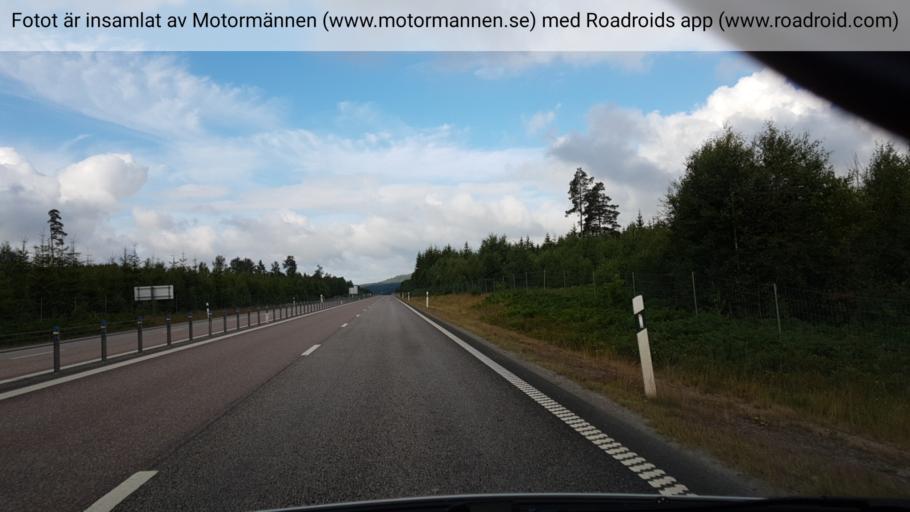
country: SE
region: Vaestra Goetaland
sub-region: Skovde Kommun
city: Skultorp
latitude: 58.3337
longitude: 13.8562
